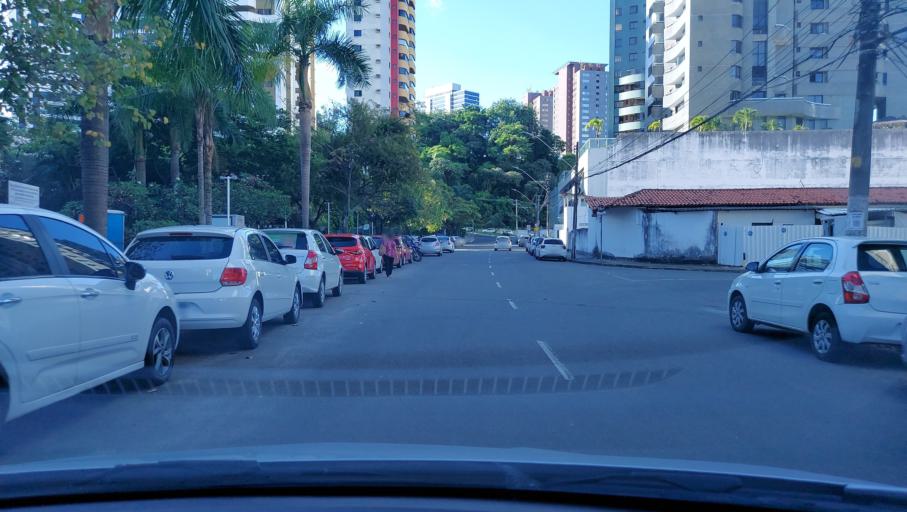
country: BR
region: Bahia
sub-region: Salvador
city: Salvador
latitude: -12.9869
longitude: -38.4522
